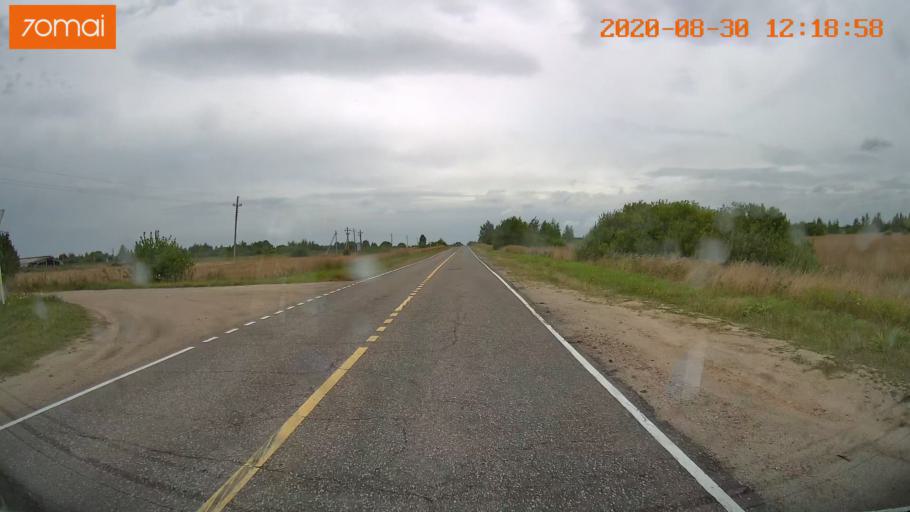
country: RU
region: Ivanovo
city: Yur'yevets
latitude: 57.3231
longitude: 42.9369
